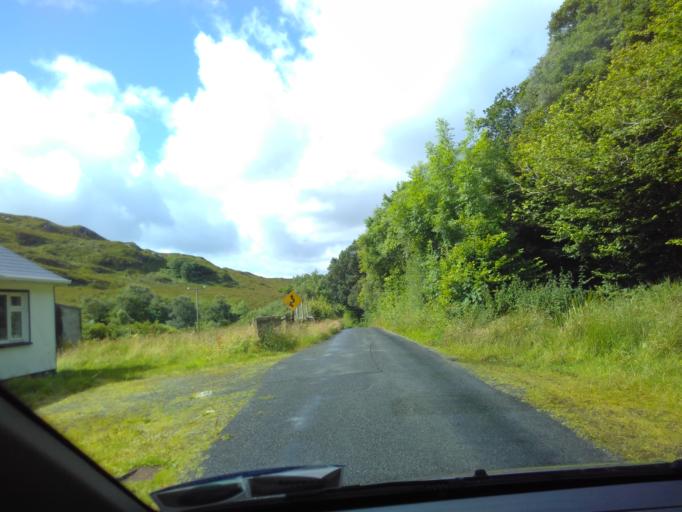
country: IE
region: Ulster
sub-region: County Donegal
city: Dunlewy
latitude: 54.9268
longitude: -8.1701
